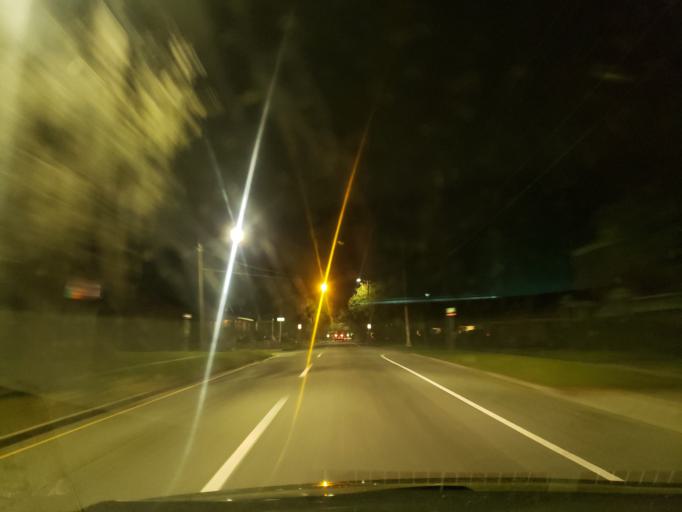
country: US
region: Georgia
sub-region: Chatham County
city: Thunderbolt
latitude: 32.0573
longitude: -81.0756
